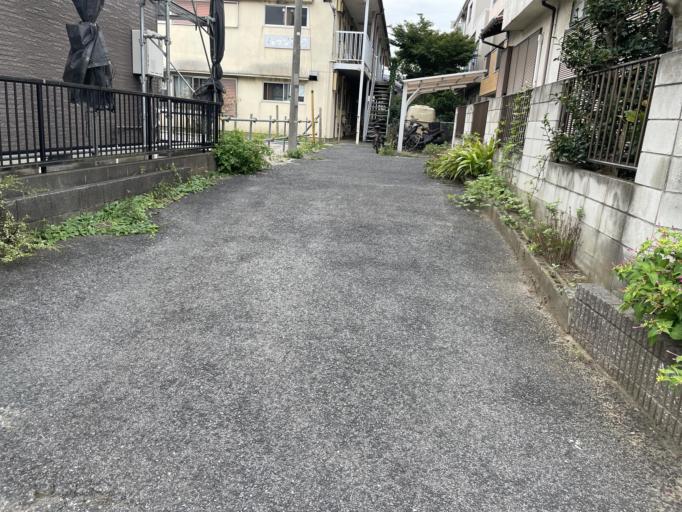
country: JP
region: Chiba
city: Nagareyama
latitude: 35.8308
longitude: 139.9195
